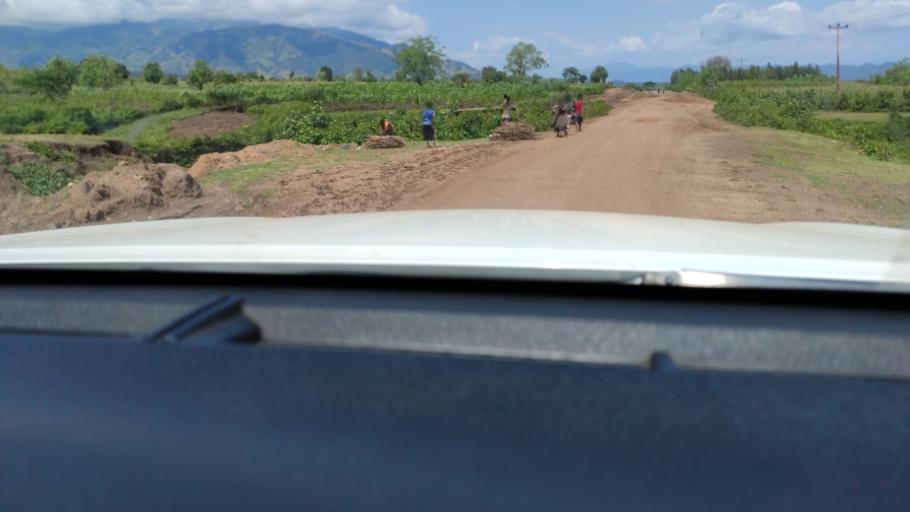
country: ET
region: Southern Nations, Nationalities, and People's Region
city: Felege Neway
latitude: 6.3658
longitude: 36.9913
